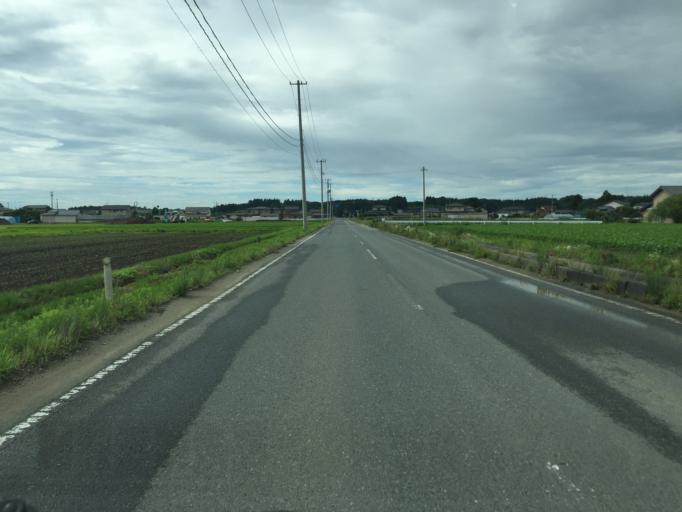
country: JP
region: Miyagi
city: Marumori
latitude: 37.7899
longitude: 140.9571
